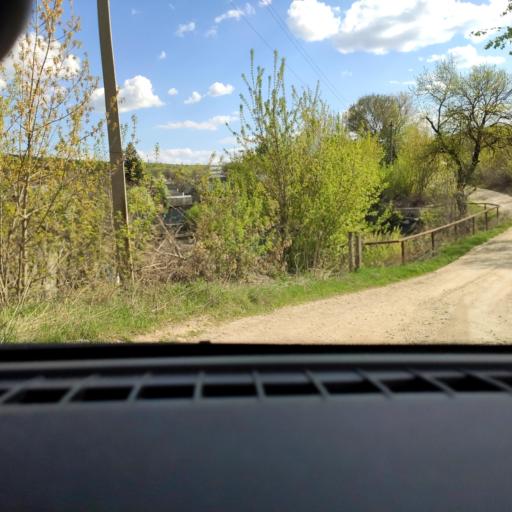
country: RU
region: Samara
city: Zhigulevsk
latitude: 53.3742
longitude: 49.5096
